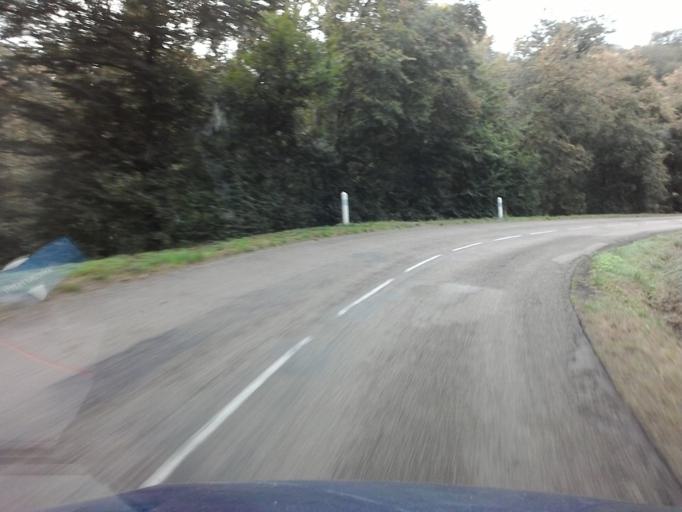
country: FR
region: Bourgogne
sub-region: Departement de la Nievre
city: Lormes
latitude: 47.2075
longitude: 3.8422
